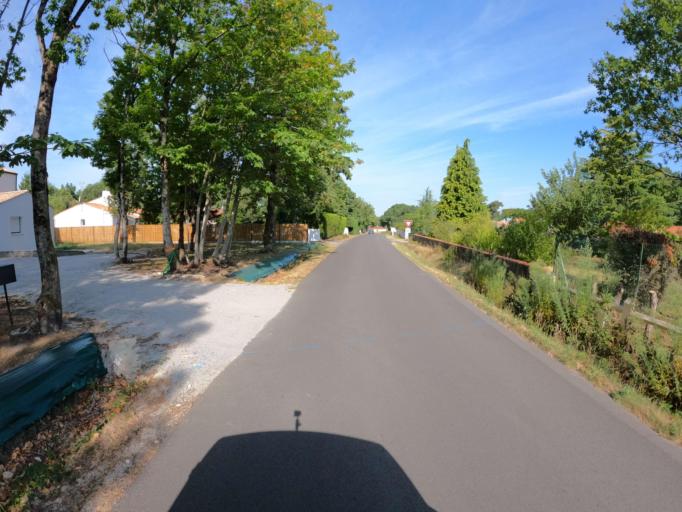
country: FR
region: Pays de la Loire
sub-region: Departement de la Vendee
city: Soullans
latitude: 46.8050
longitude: -1.8787
